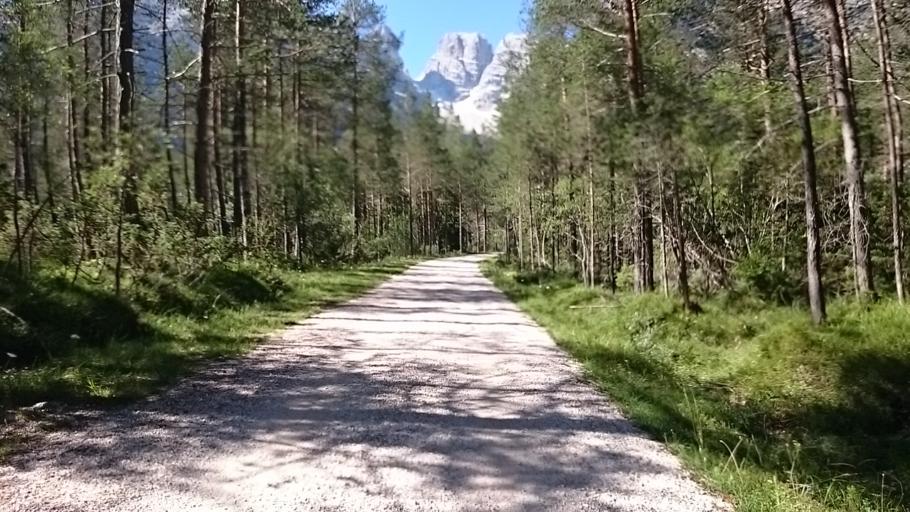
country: IT
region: Trentino-Alto Adige
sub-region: Bolzano
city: Dobbiaco
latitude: 46.6197
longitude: 12.2227
